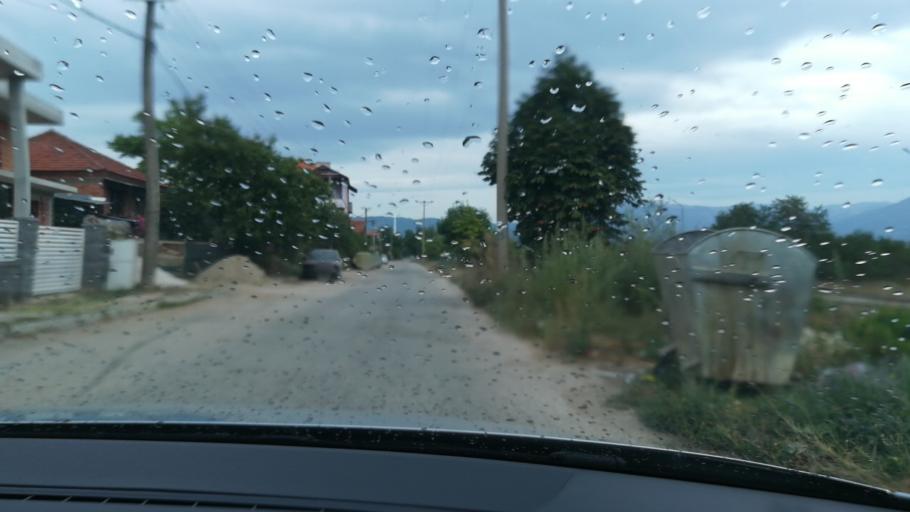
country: MK
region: Kicevo
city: Kicevo
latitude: 41.5132
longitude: 20.9495
